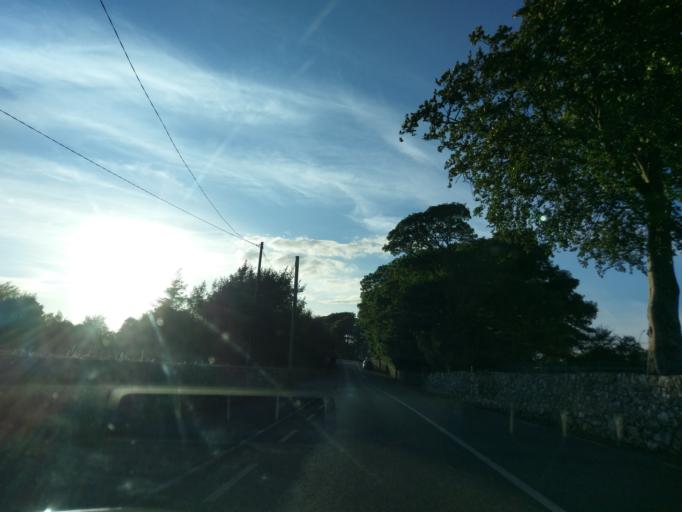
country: IE
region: Connaught
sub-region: County Galway
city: Athenry
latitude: 53.2989
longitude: -8.7592
